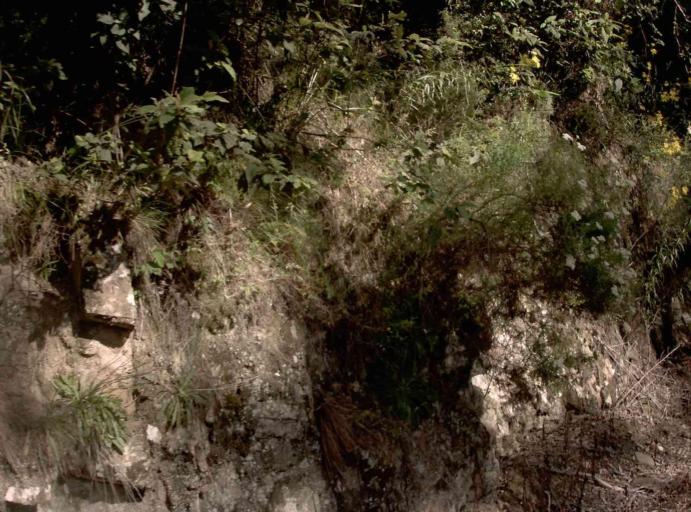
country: AU
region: Victoria
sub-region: East Gippsland
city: Lakes Entrance
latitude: -37.4934
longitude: 148.5555
